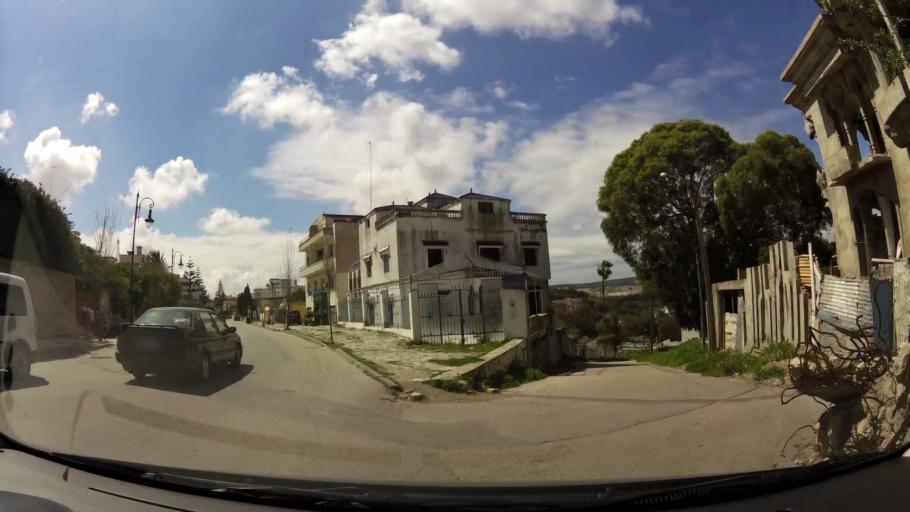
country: MA
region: Tanger-Tetouan
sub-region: Tanger-Assilah
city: Tangier
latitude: 35.7781
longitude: -5.8366
